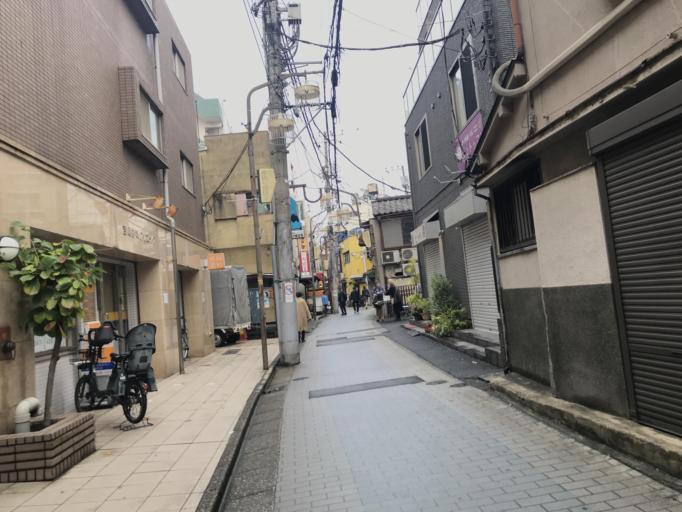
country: JP
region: Chiba
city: Funabashi
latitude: 35.6987
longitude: 139.9872
